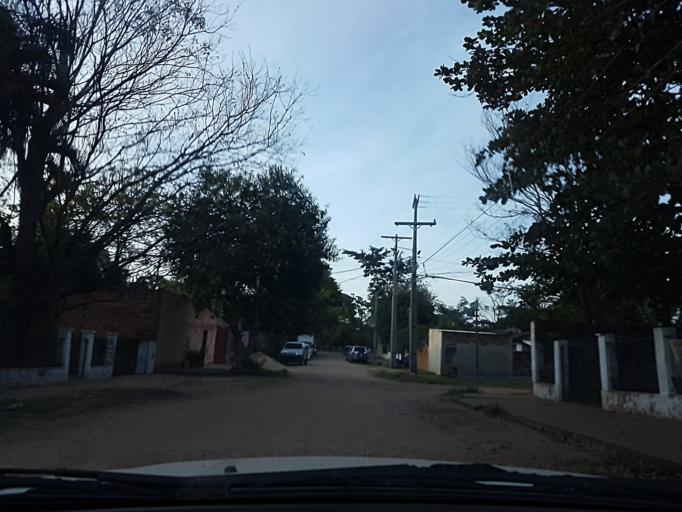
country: PY
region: Central
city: Colonia Mariano Roque Alonso
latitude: -25.1984
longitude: -57.5456
